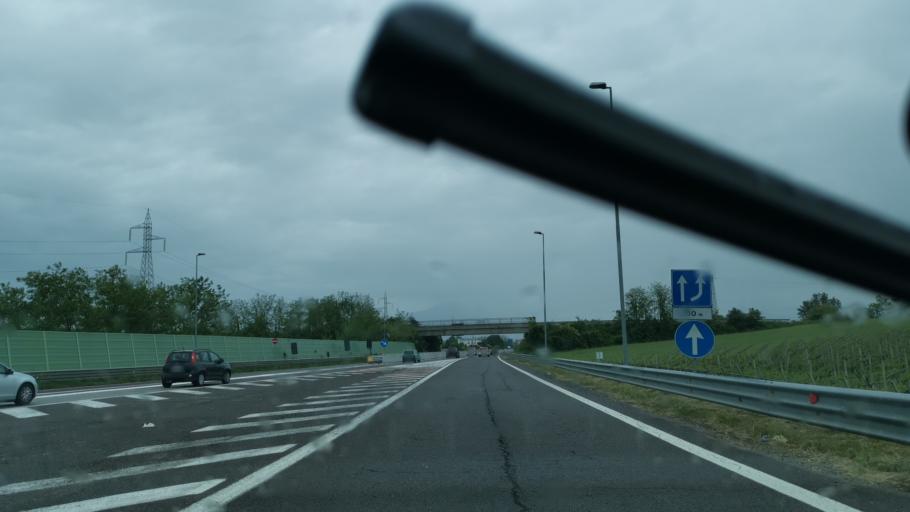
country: IT
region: Veneto
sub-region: Provincia di Verona
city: Castelnuovo del Garda
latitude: 45.4400
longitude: 10.7439
